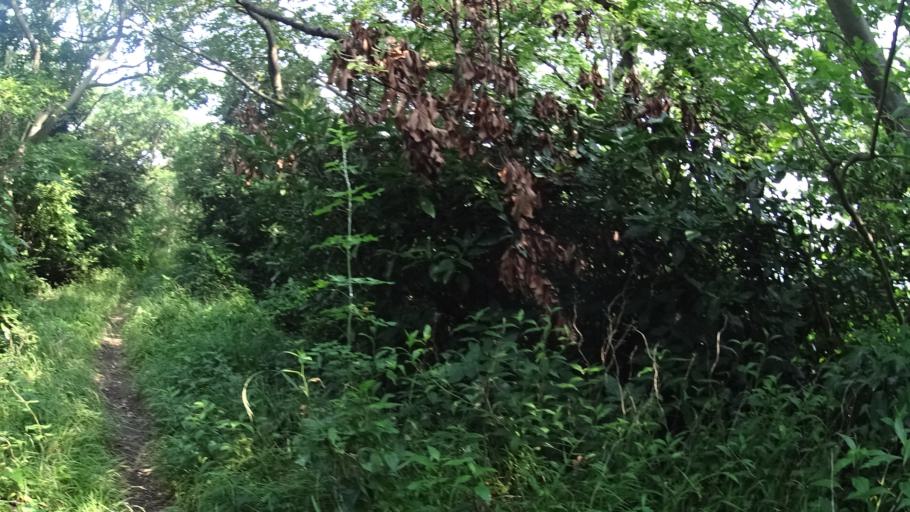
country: JP
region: Kanagawa
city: Zushi
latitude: 35.3032
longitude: 139.6165
